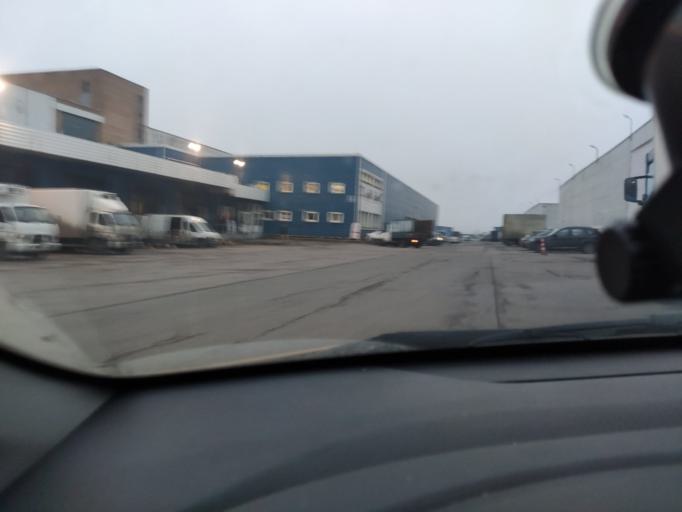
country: RU
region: Moskovskaya
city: Biryulevo Zapadnoye
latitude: 55.5923
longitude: 37.6222
